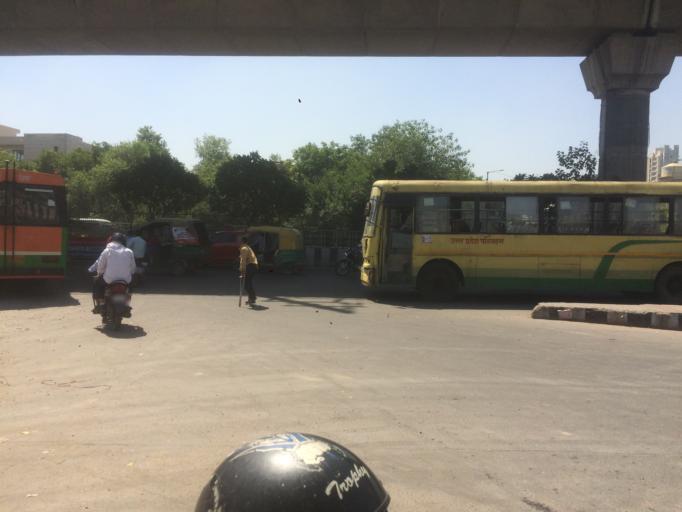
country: IN
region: Uttar Pradesh
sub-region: Gautam Buddha Nagar
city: Noida
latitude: 28.5758
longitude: 77.3573
